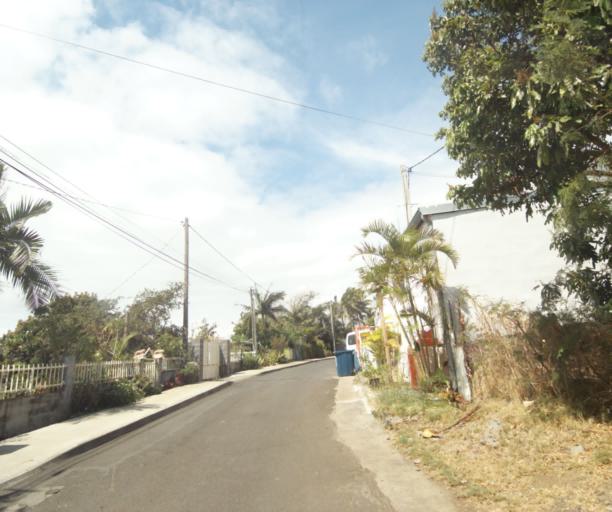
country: RE
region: Reunion
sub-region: Reunion
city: Saint-Paul
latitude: -21.0549
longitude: 55.2571
